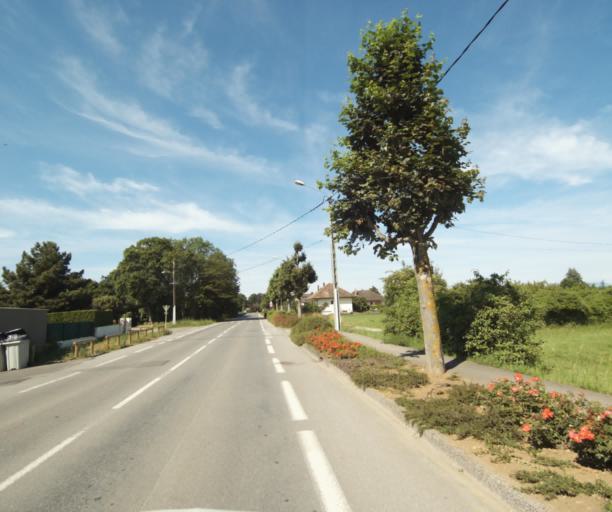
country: FR
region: Rhone-Alpes
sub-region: Departement de la Haute-Savoie
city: Thonon-les-Bains
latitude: 46.3868
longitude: 6.5010
